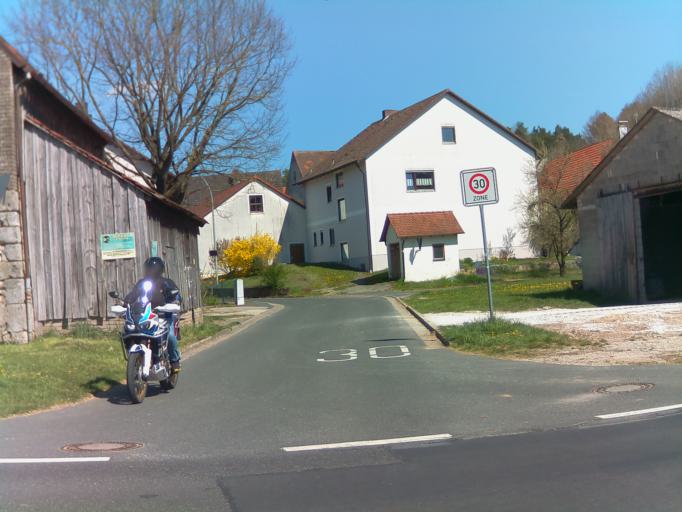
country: DE
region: Bavaria
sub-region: Upper Palatinate
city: Illschwang
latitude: 49.4892
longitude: 11.6490
